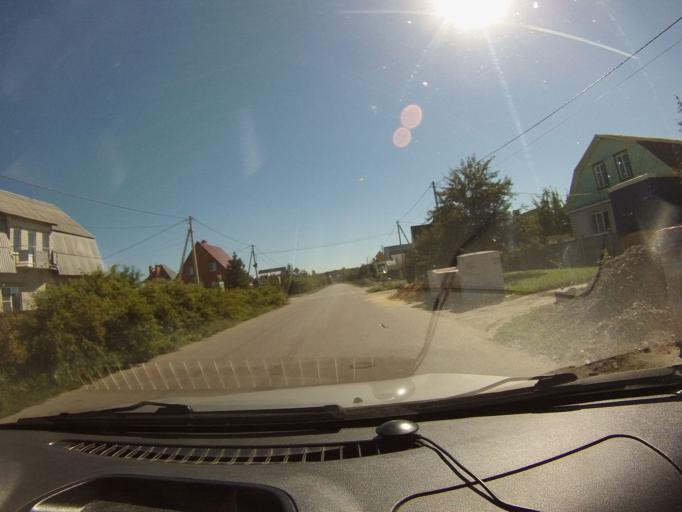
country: RU
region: Tambov
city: Komsomolets
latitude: 52.7643
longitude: 41.3628
